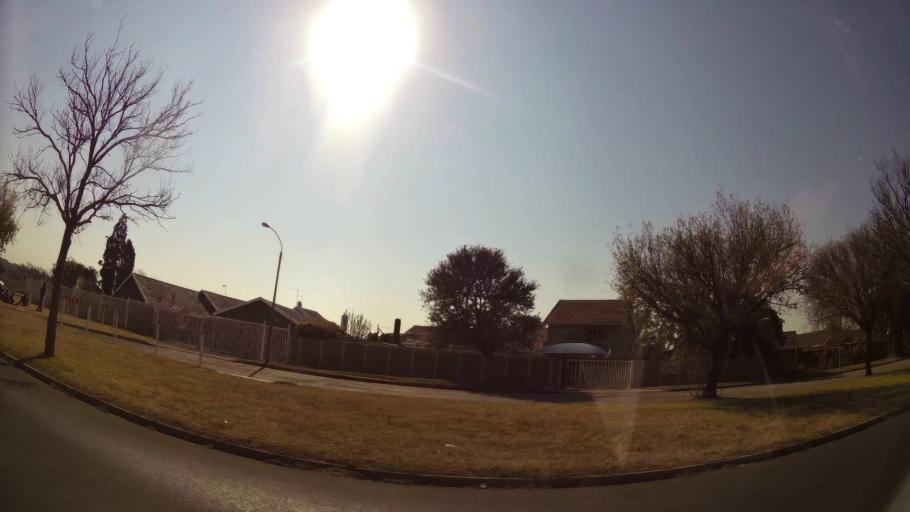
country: ZA
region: Gauteng
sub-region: Ekurhuleni Metropolitan Municipality
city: Boksburg
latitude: -26.2416
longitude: 28.2648
